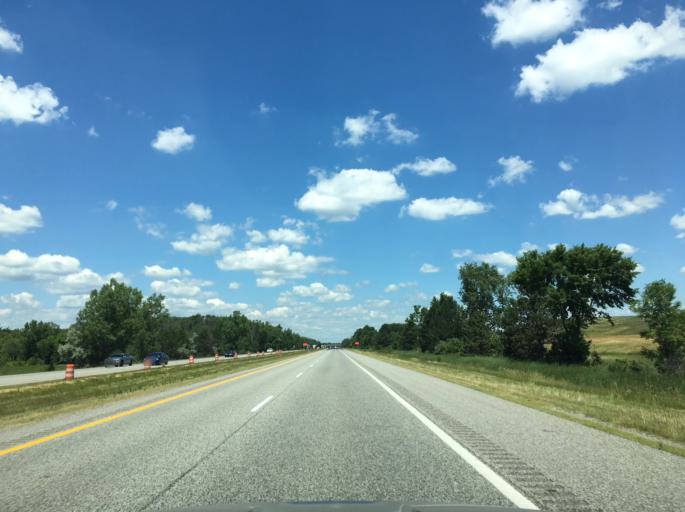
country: US
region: Michigan
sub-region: Midland County
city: Midland
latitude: 43.6287
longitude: -84.1784
